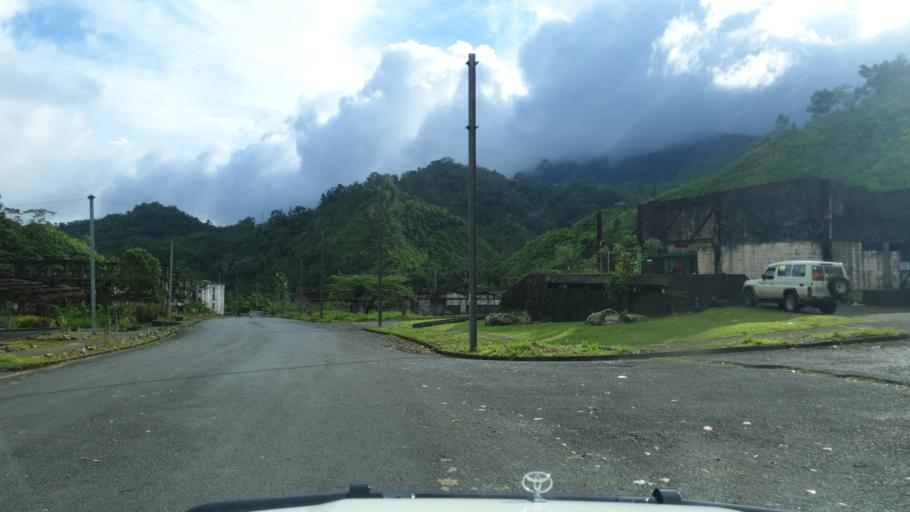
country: PG
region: Bougainville
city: Panguna
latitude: -6.3031
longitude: 155.4905
